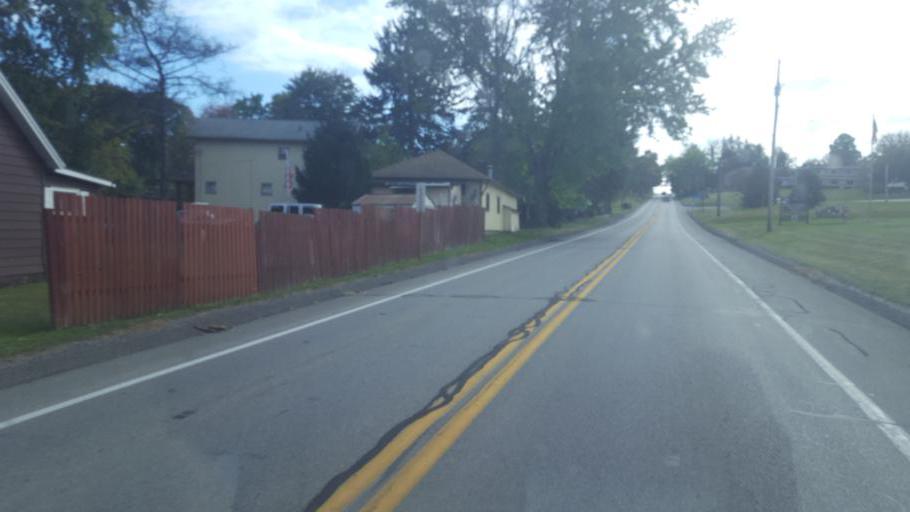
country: US
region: Pennsylvania
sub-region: Mercer County
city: Mercer
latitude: 41.2337
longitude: -80.2385
